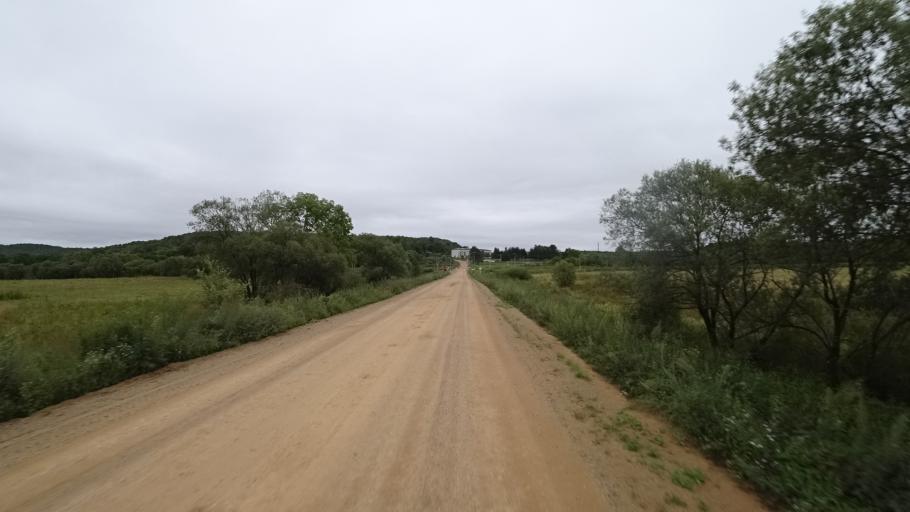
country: RU
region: Primorskiy
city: Rettikhovka
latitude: 44.1756
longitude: 132.8772
